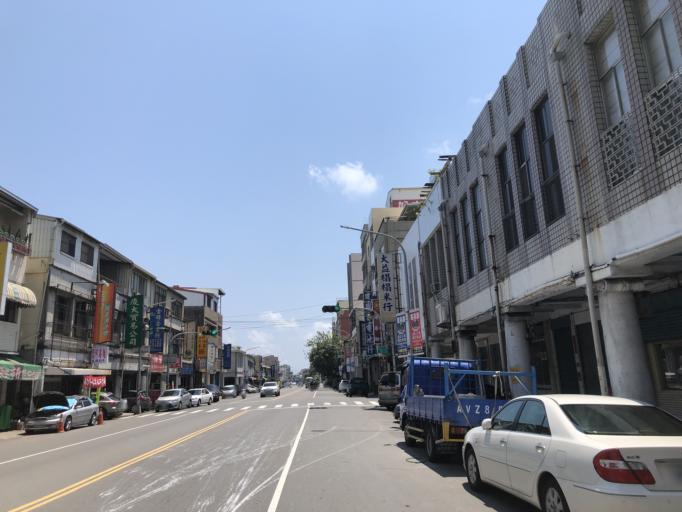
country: TW
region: Kaohsiung
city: Kaohsiung
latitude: 22.6260
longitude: 120.2778
